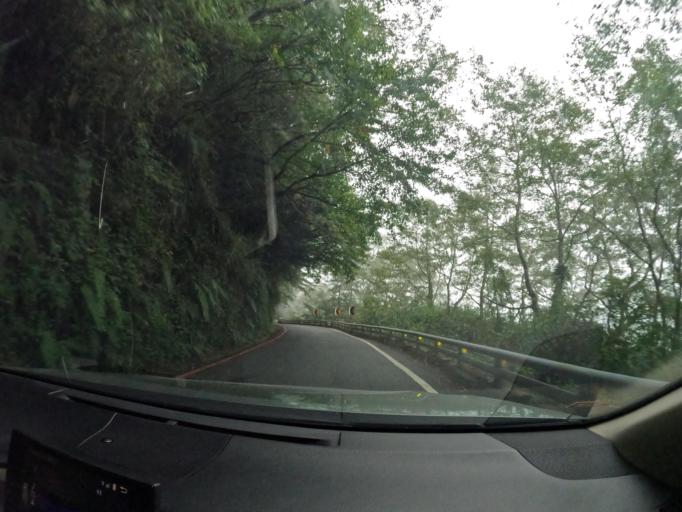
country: TW
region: Taiwan
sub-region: Taitung
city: Taitung
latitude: 23.2435
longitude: 120.9840
